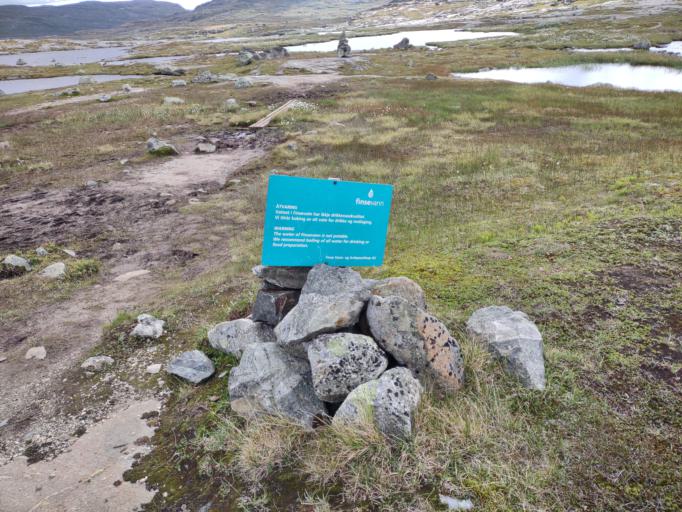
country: NO
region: Sogn og Fjordane
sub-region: Aurland
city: Aurlandsvangen
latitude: 60.5931
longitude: 7.5096
